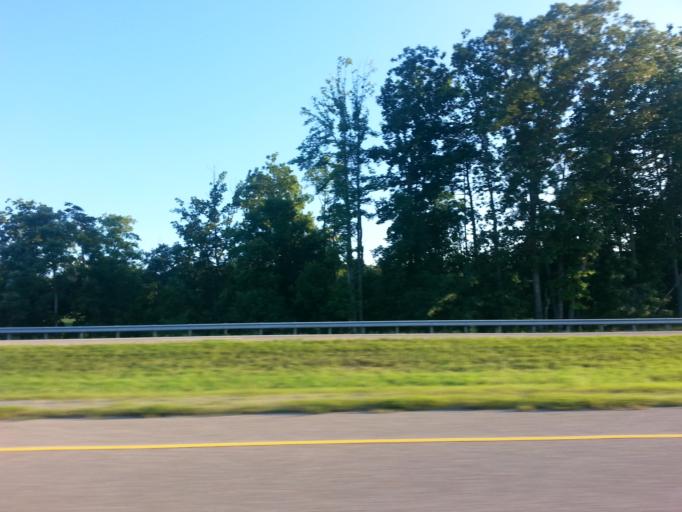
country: US
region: Tennessee
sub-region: Loudon County
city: Lenoir City
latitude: 35.7589
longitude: -84.2229
